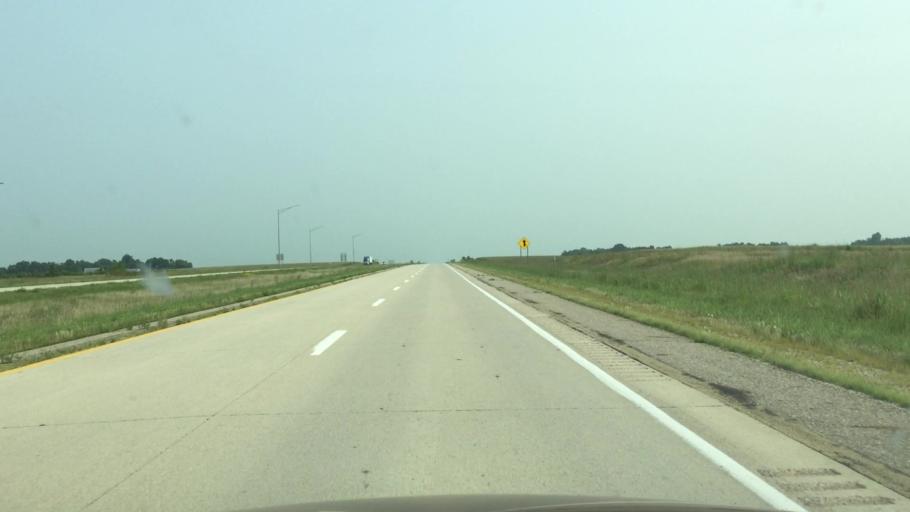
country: US
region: Iowa
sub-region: Osceola County
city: Sibley
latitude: 43.4068
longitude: -95.7170
